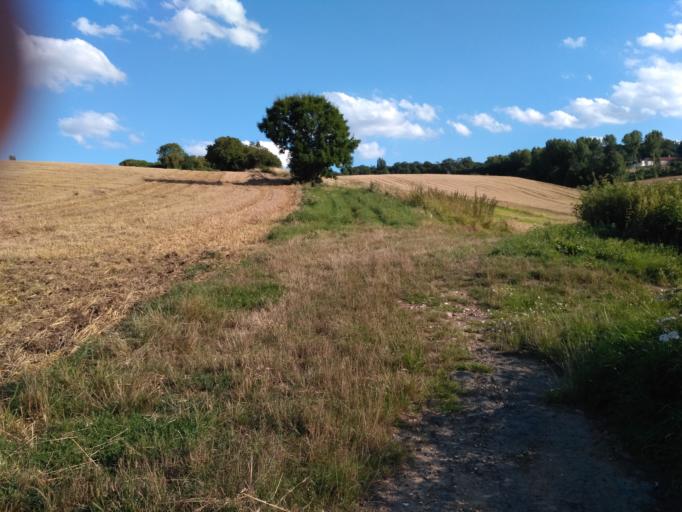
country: FR
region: Ile-de-France
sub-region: Departement du Val-d'Oise
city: Maffliers
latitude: 49.0963
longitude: 2.2803
